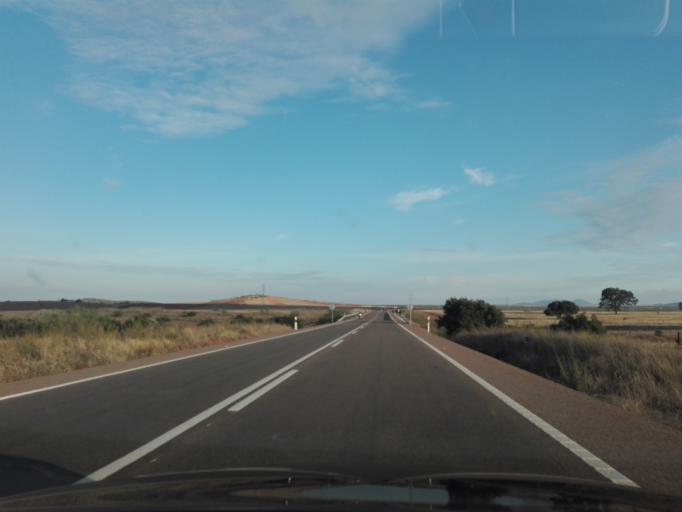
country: ES
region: Extremadura
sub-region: Provincia de Badajoz
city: Usagre
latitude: 38.3627
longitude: -6.2256
